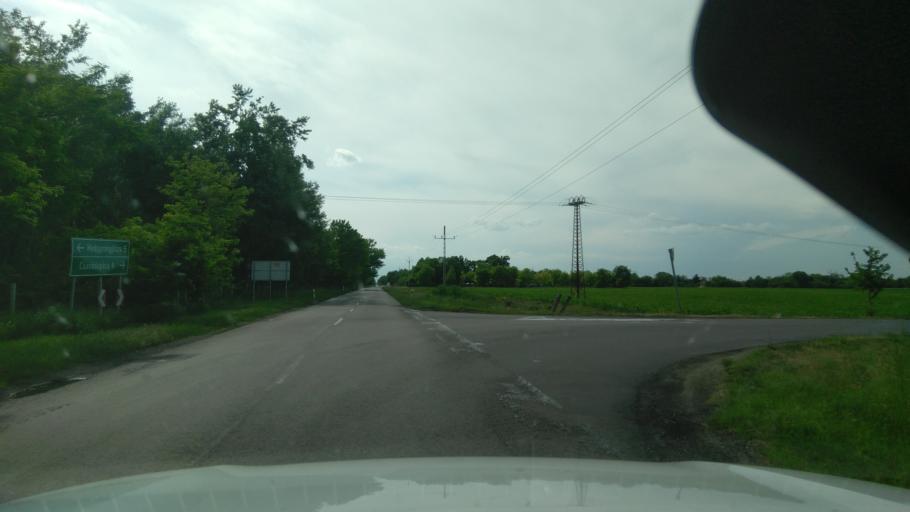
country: HU
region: Bekes
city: Medgyesegyhaza
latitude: 46.5141
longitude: 20.9748
